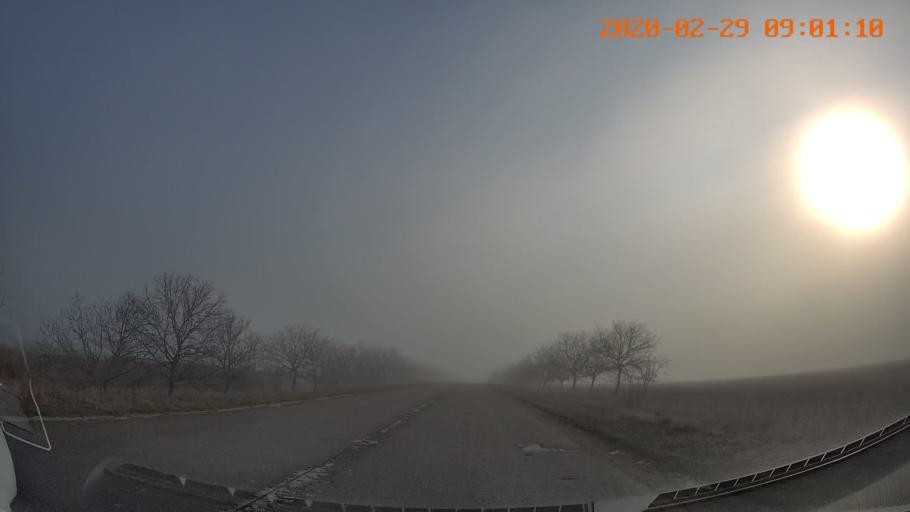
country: UA
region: Odessa
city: Velykoploske
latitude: 46.9234
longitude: 29.6874
